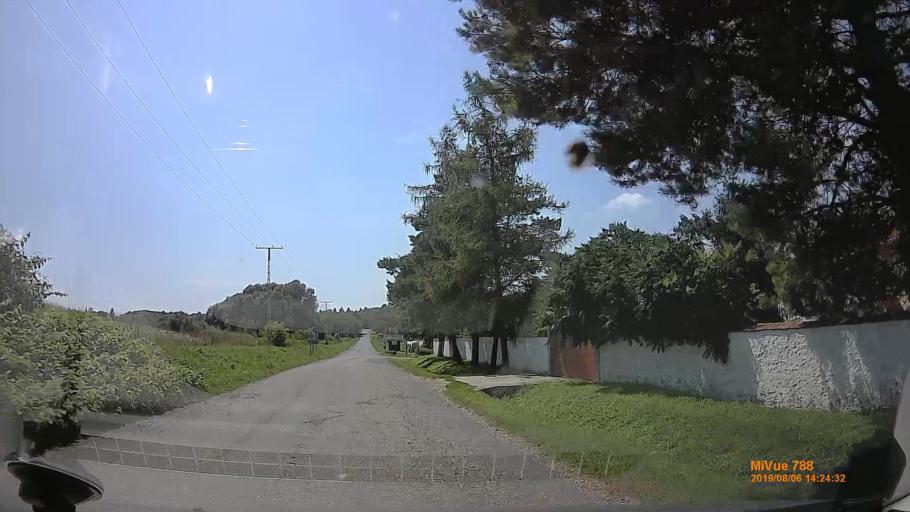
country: HU
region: Zala
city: Nagykanizsa
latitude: 46.4965
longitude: 17.0605
